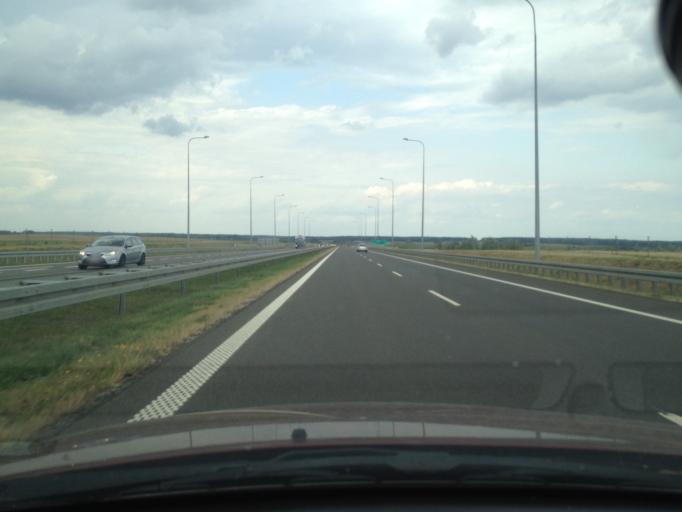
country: PL
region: West Pomeranian Voivodeship
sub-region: Powiat pyrzycki
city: Bielice
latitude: 53.1268
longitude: 14.7347
